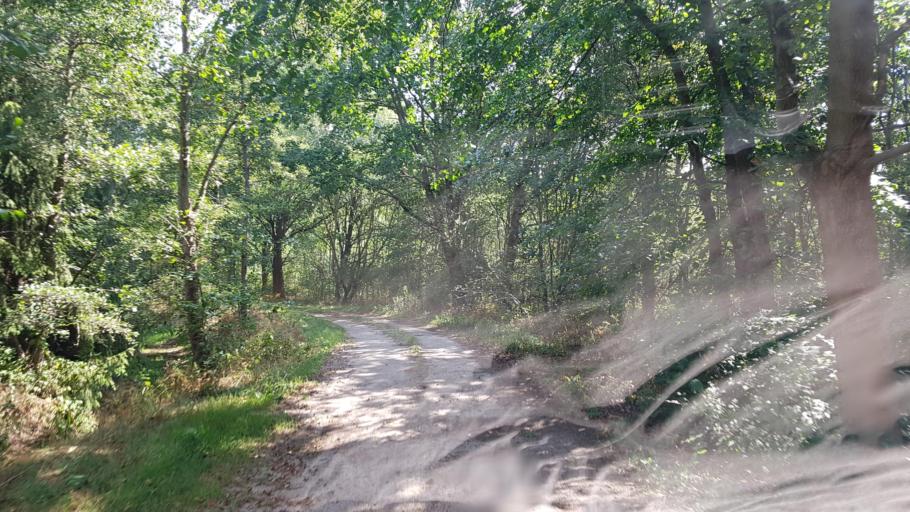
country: DE
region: Brandenburg
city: Bruck
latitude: 52.1927
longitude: 12.8060
